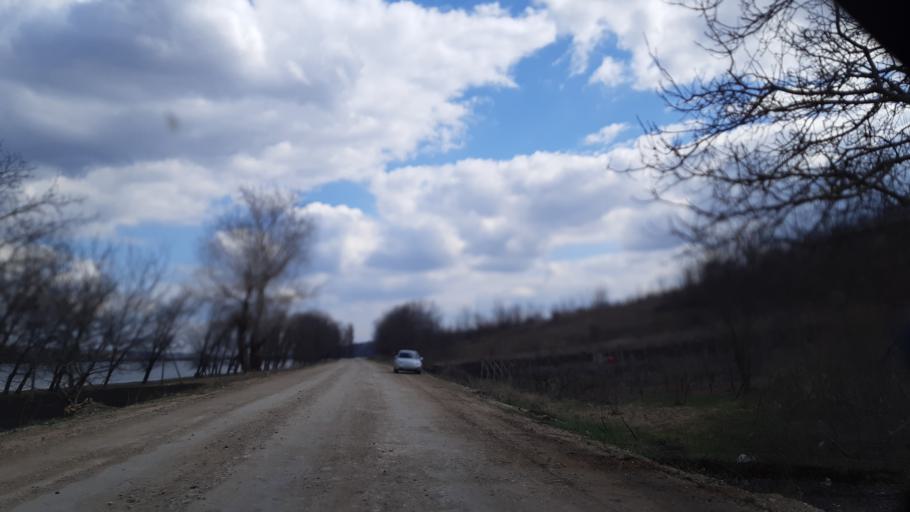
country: MD
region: Laloveni
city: Ialoveni
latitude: 46.8890
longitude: 28.7319
